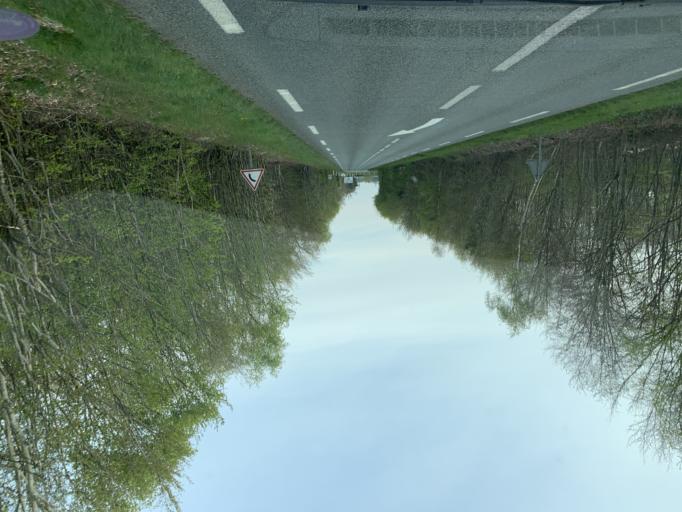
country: FR
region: Haute-Normandie
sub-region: Departement de la Seine-Maritime
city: La Mailleraye-sur-Seine
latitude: 49.4593
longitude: 0.7831
